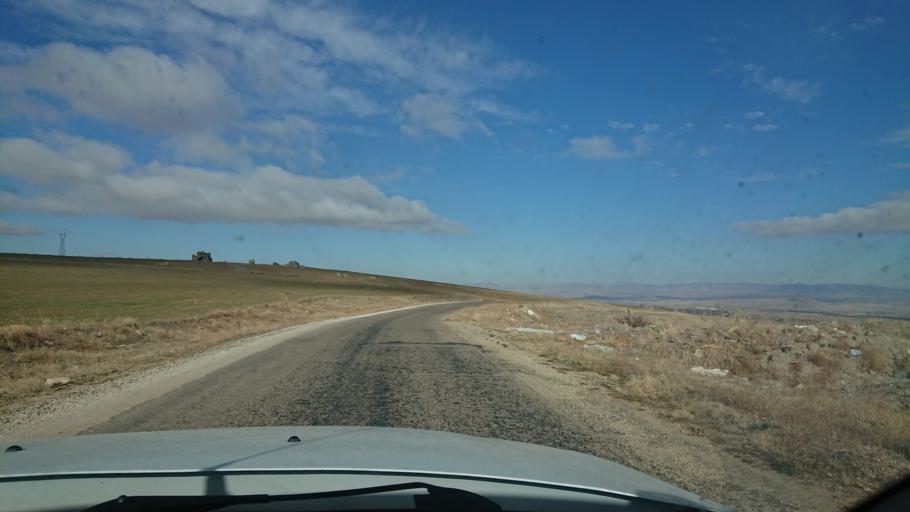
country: TR
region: Aksaray
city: Agacoren
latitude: 38.8396
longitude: 33.9530
